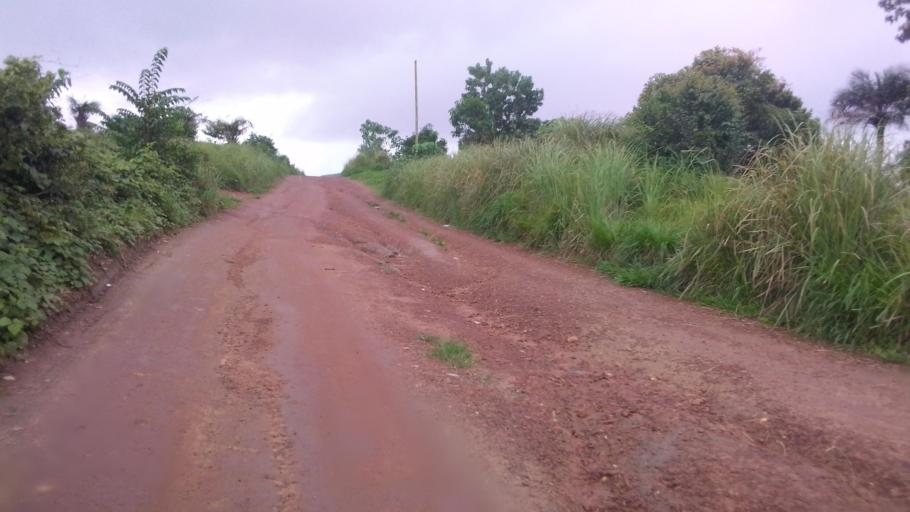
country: SL
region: Eastern Province
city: Kenema
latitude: 7.8416
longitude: -11.1799
